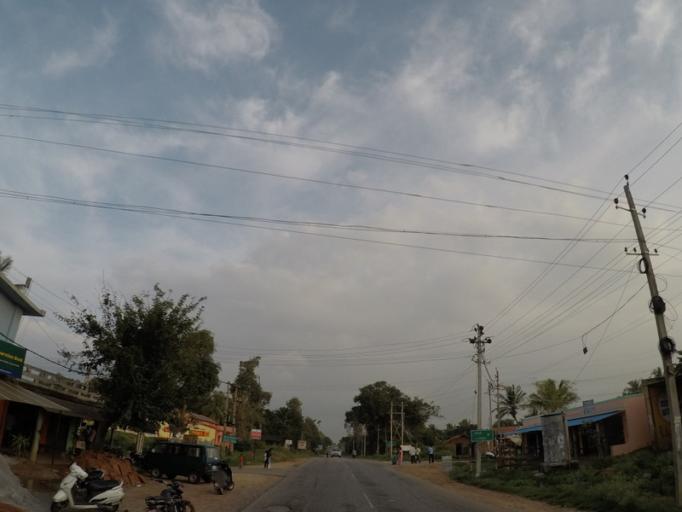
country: IN
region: Karnataka
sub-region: Hassan
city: Hassan
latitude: 13.0536
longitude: 76.0535
